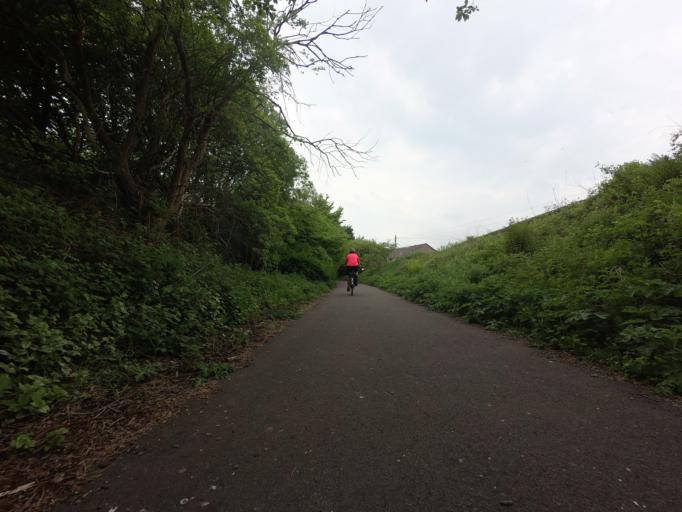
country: GB
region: Scotland
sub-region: Fife
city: Townhill
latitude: 56.0864
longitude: -3.4416
